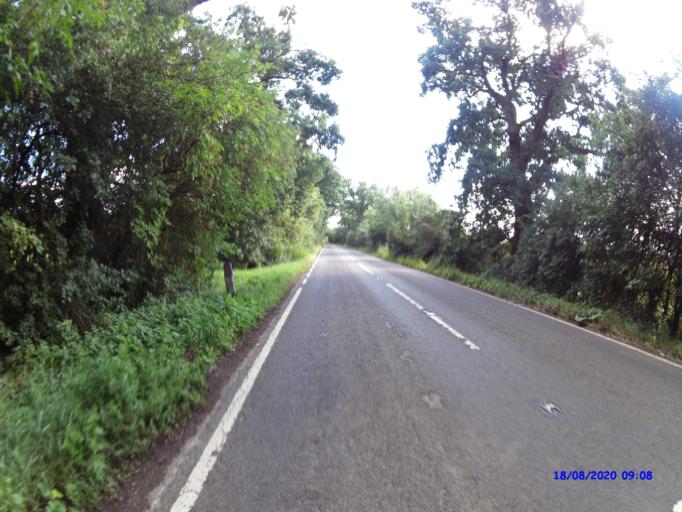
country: GB
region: England
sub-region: Cambridgeshire
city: Ramsey
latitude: 52.4675
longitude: -0.0949
